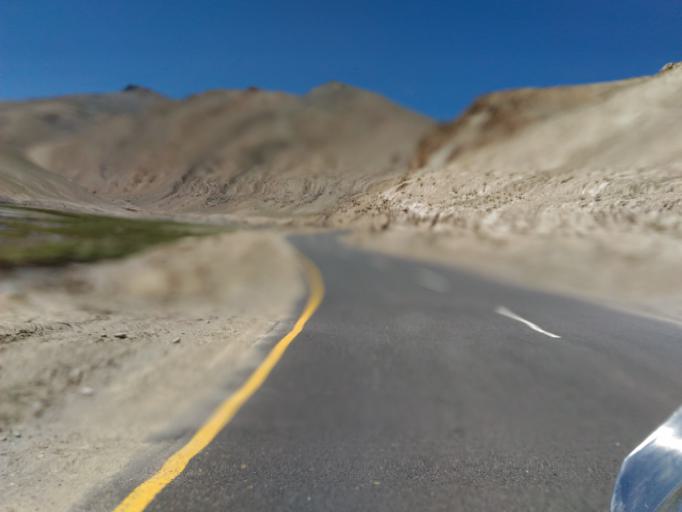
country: IN
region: Kashmir
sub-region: Ladakh
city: Leh
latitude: 33.5941
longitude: 77.7540
